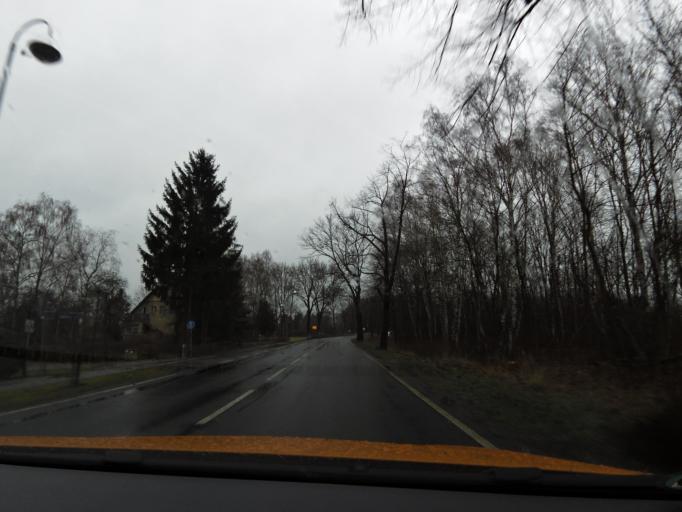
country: DE
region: Brandenburg
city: Zossen
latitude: 52.2541
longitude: 13.4482
